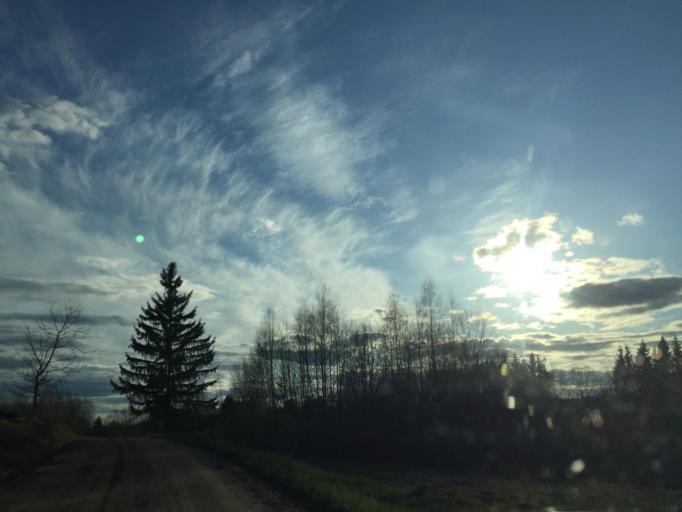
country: LV
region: Rezekne
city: Rezekne
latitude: 56.5808
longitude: 27.3402
